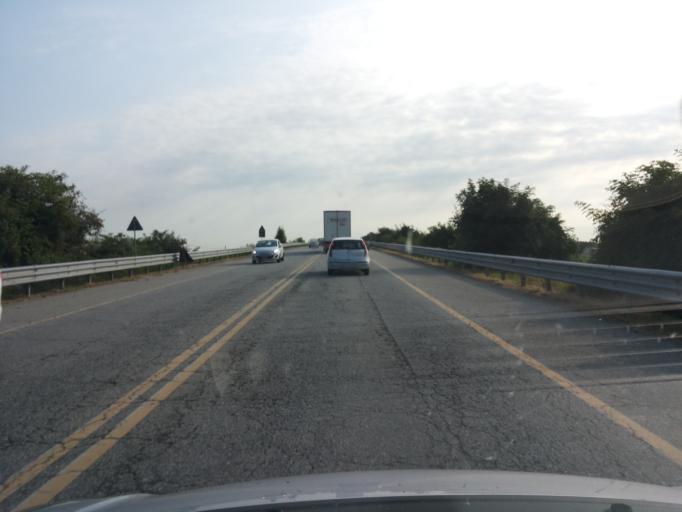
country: IT
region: Piedmont
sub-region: Provincia di Vercelli
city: Desana
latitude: 45.2905
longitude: 8.3814
